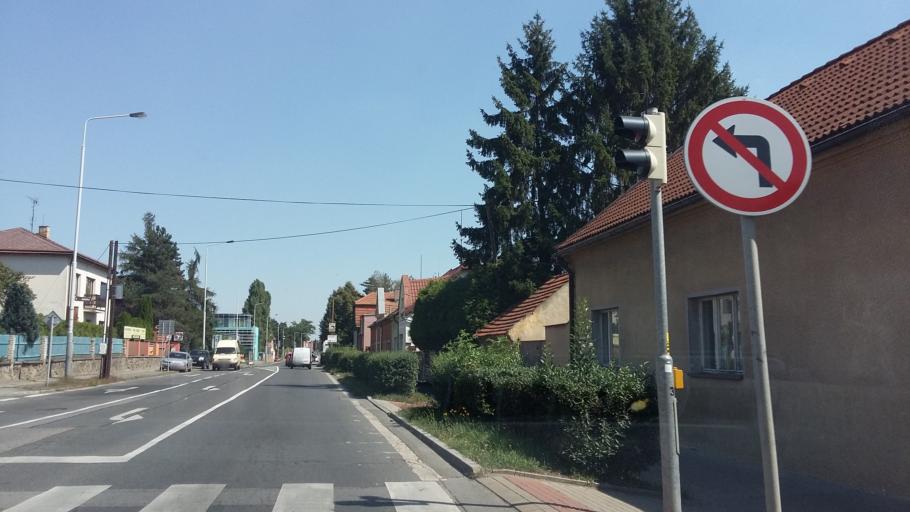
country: CZ
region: Praha
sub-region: Praha 20
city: Horni Pocernice
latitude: 50.1127
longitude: 14.5977
